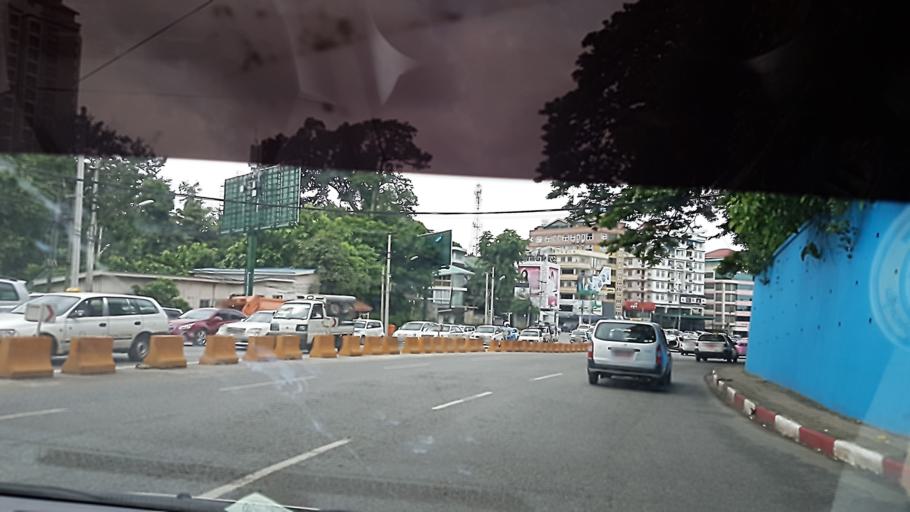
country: MM
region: Yangon
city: Yangon
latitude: 16.8110
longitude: 96.1561
